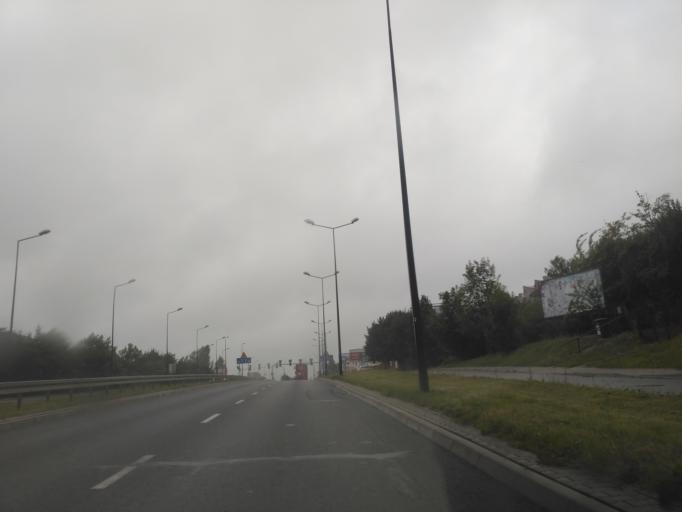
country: PL
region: Lublin Voivodeship
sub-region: Powiat lubelski
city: Lublin
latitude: 51.2735
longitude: 22.5737
